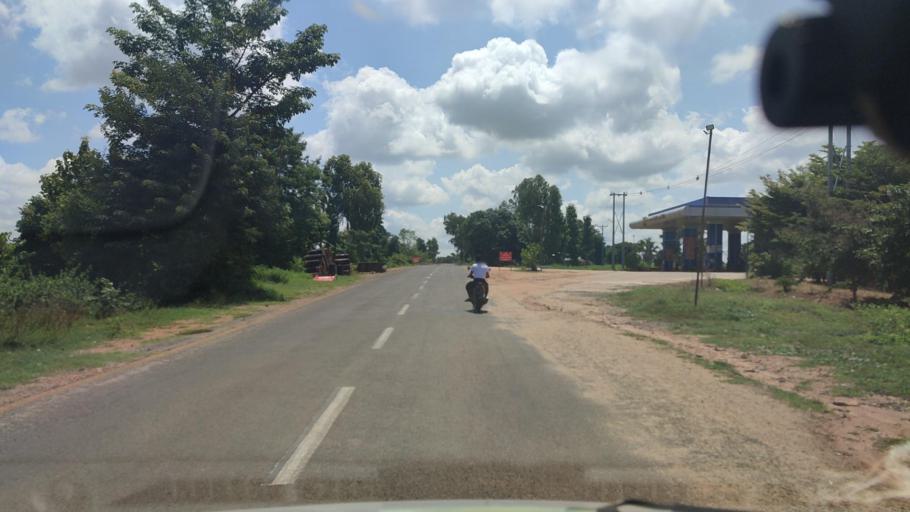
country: MM
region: Magway
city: Magway
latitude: 20.1907
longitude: 95.0560
